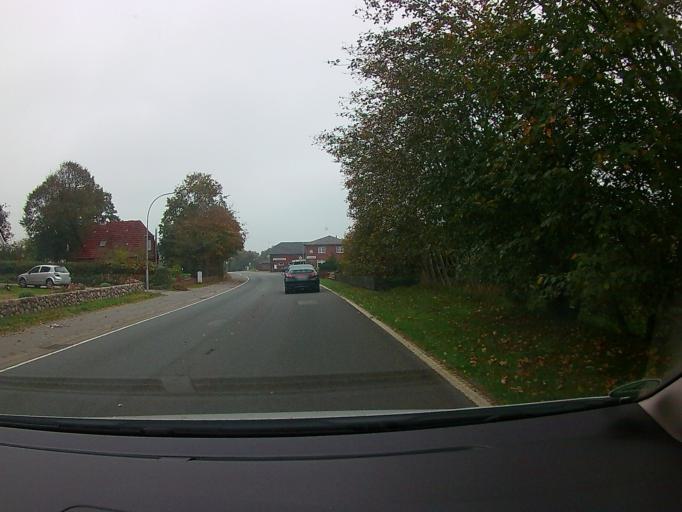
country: DE
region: Schleswig-Holstein
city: Sonnebull
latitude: 54.6260
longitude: 8.9942
